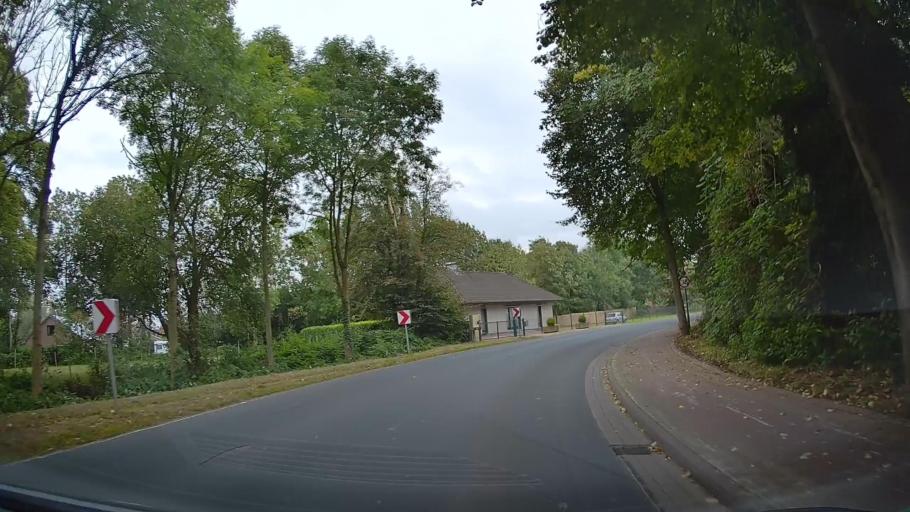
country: DE
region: Lower Saxony
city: Wischhafen
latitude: 53.7922
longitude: 9.3245
